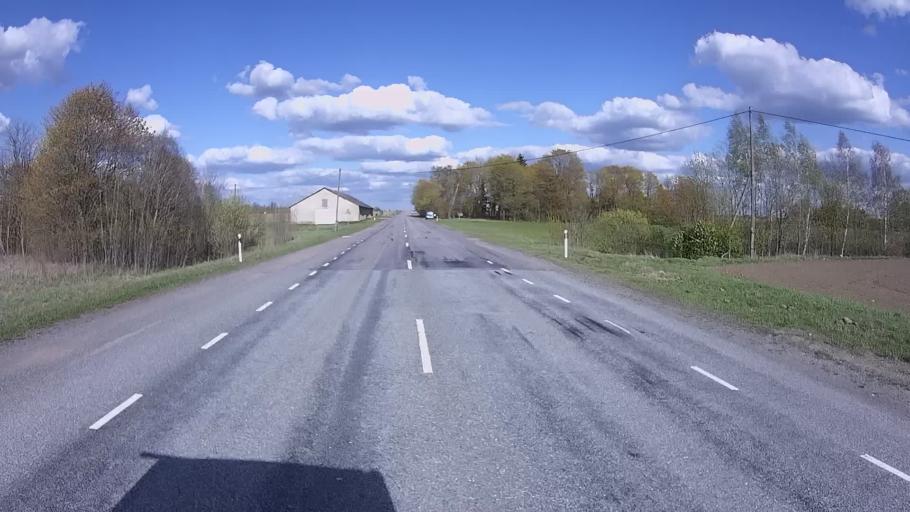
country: EE
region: Jogevamaa
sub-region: Poltsamaa linn
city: Poltsamaa
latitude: 58.6862
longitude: 26.0979
